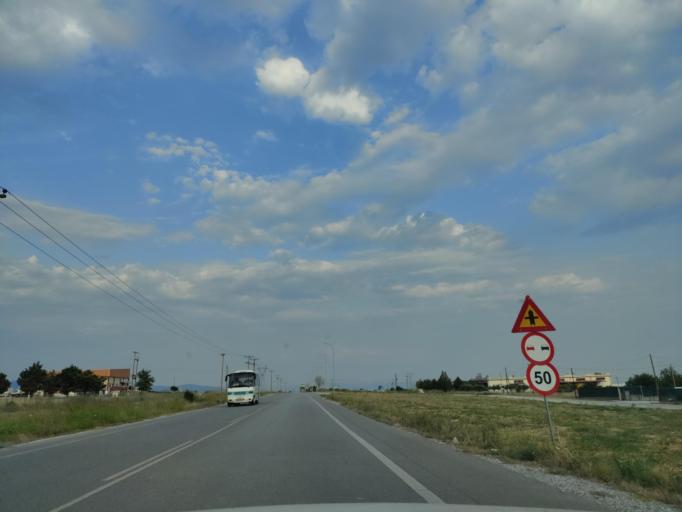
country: GR
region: East Macedonia and Thrace
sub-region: Nomos Dramas
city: Petroussa
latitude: 41.1780
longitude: 23.9982
